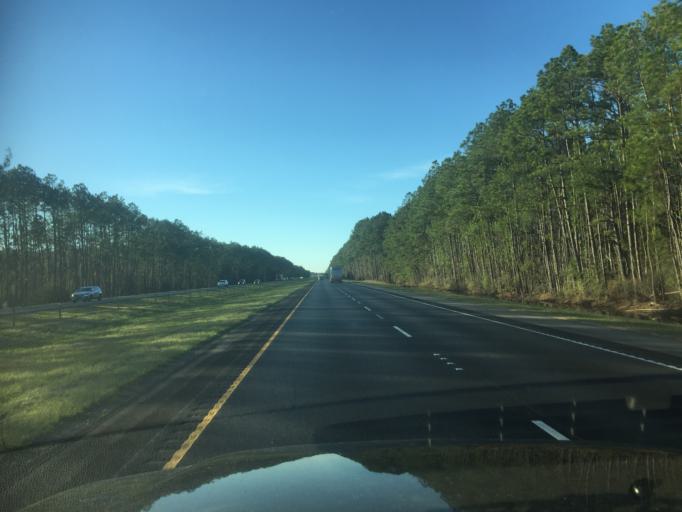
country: US
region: Louisiana
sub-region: Saint Tammany Parish
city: Lacombe
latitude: 30.3812
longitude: -89.9768
